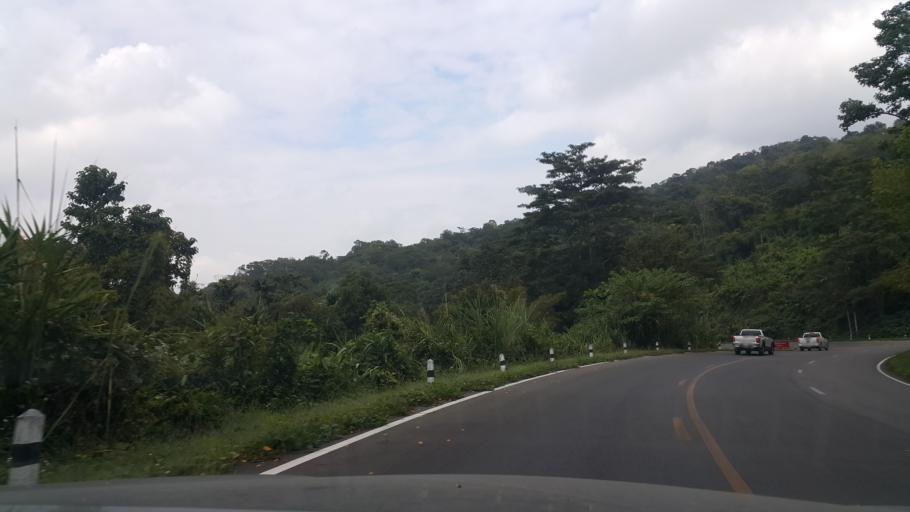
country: TH
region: Phayao
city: Phayao
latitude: 19.0575
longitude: 99.7892
